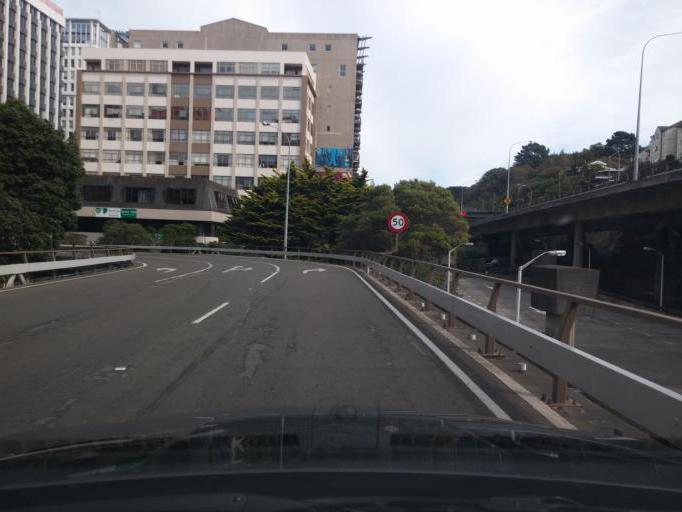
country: NZ
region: Wellington
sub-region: Wellington City
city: Wellington
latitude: -41.2837
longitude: 174.7739
